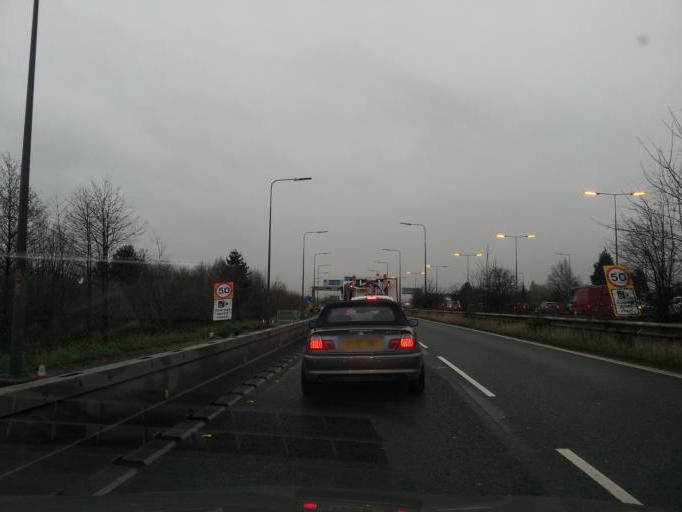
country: GB
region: England
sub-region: Manchester
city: Swinton
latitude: 53.4803
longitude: -2.3753
